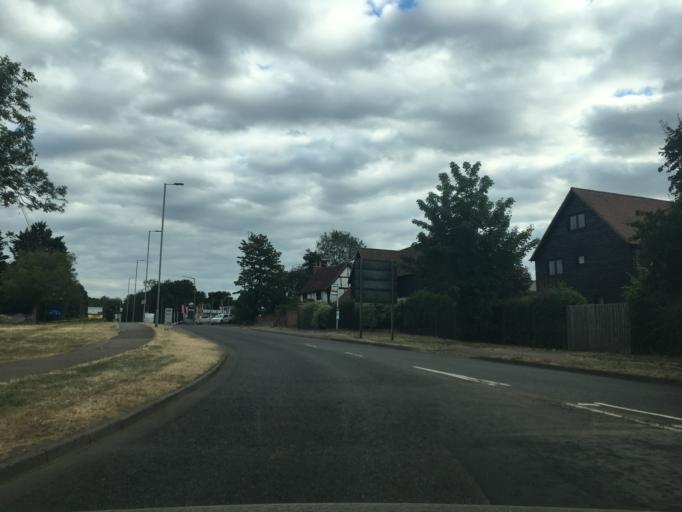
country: GB
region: England
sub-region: Hertfordshire
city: Hemel Hempstead
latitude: 51.7704
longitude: -0.4489
